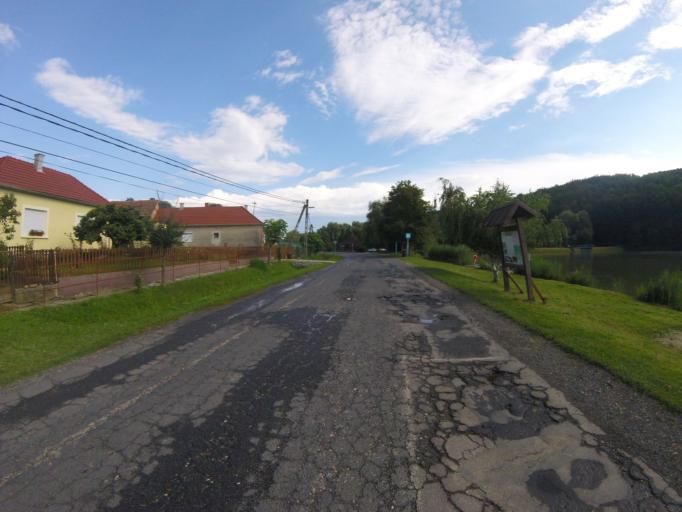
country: HU
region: Zala
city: Becsehely
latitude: 46.4930
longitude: 16.7433
